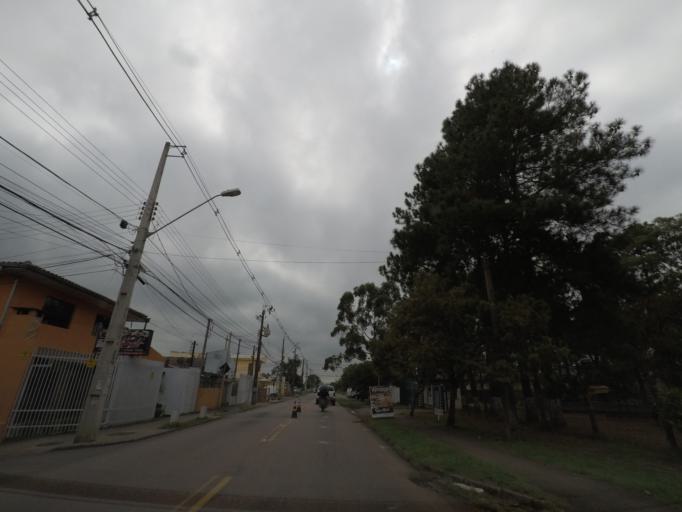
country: BR
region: Parana
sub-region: Curitiba
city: Curitiba
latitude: -25.4981
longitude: -49.3351
